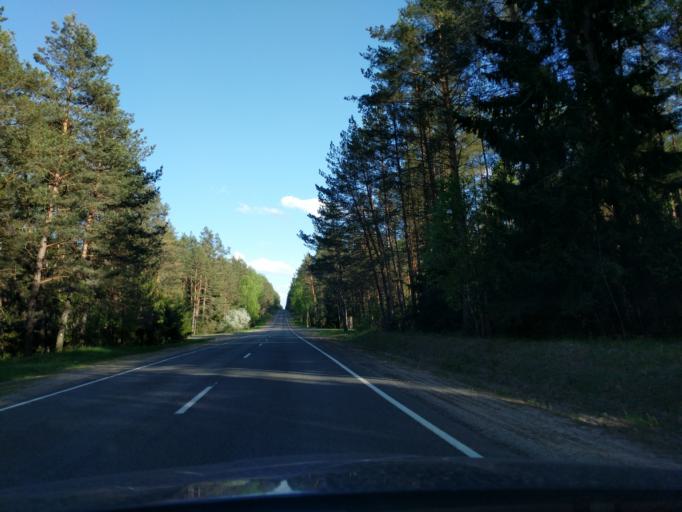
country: BY
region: Minsk
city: Myadzyel
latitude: 54.8042
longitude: 26.9951
